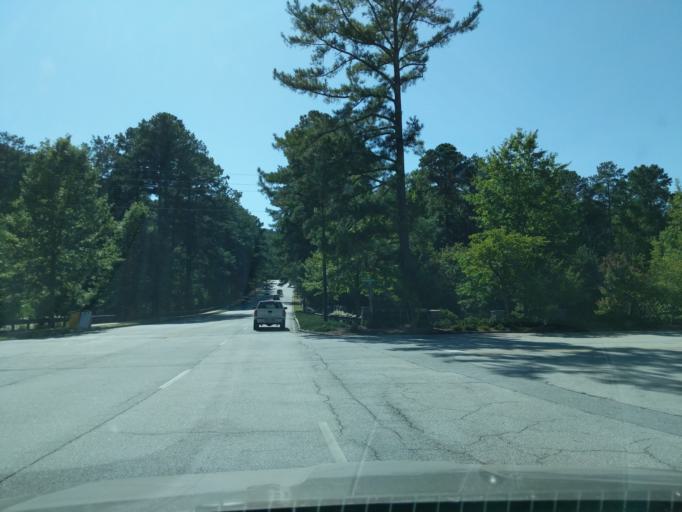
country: US
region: Georgia
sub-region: DeKalb County
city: Stone Mountain
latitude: 33.8139
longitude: -84.1471
